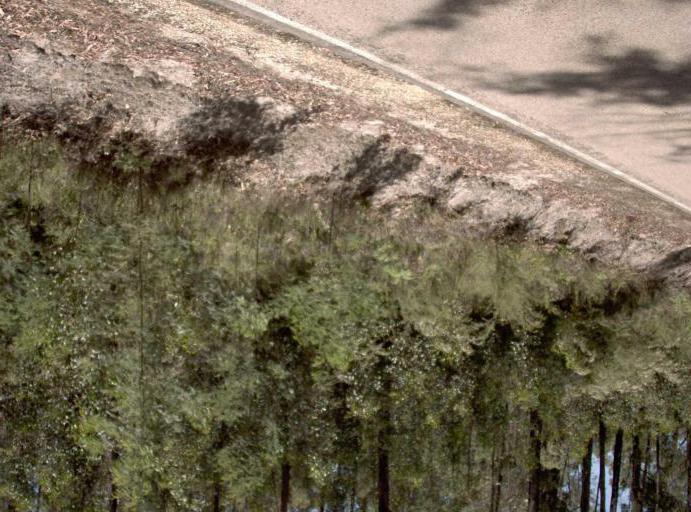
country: AU
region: Victoria
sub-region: East Gippsland
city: Lakes Entrance
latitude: -37.6469
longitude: 147.8938
